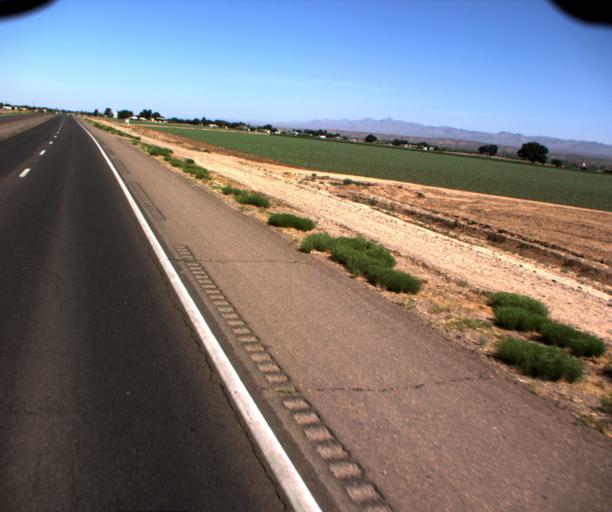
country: US
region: Arizona
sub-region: Graham County
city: Pima
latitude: 32.8816
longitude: -109.8078
